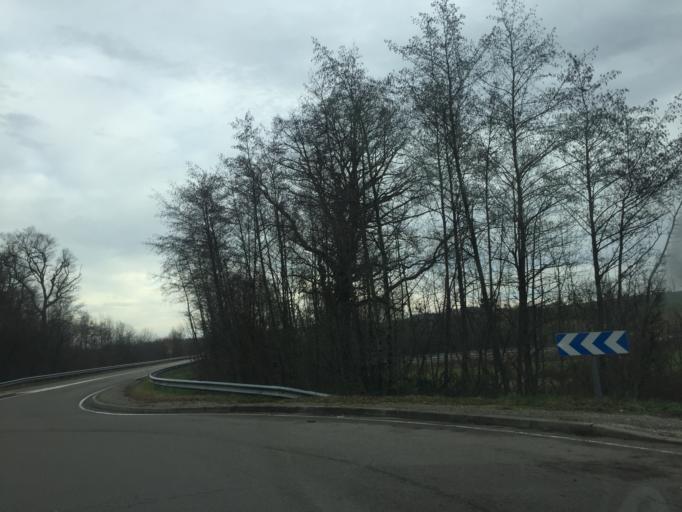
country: FR
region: Franche-Comte
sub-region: Departement du Jura
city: Poligny
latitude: 46.8461
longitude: 5.5755
